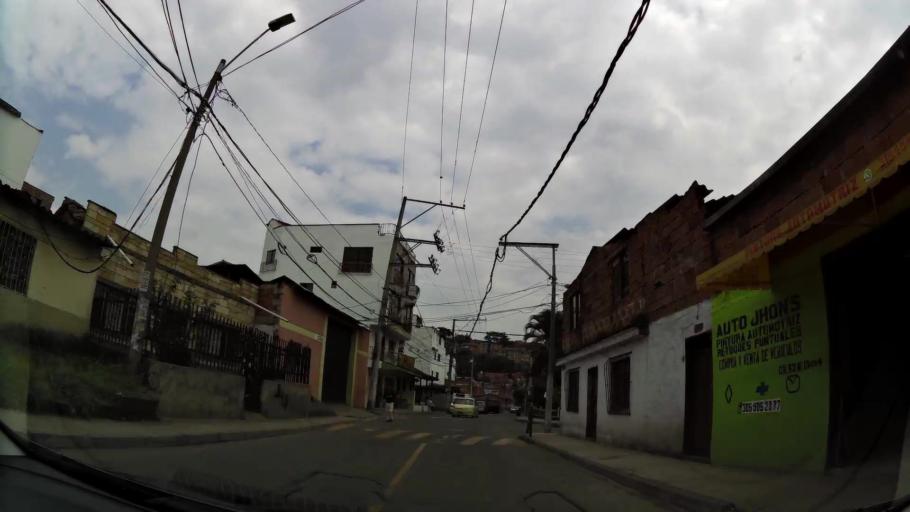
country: CO
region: Antioquia
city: Itagui
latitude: 6.1956
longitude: -75.5923
